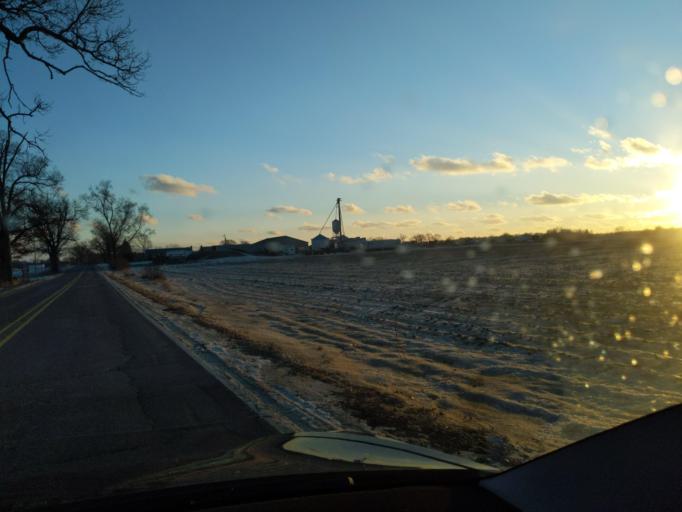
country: US
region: Michigan
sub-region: Ingham County
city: Stockbridge
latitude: 42.4530
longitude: -84.2099
